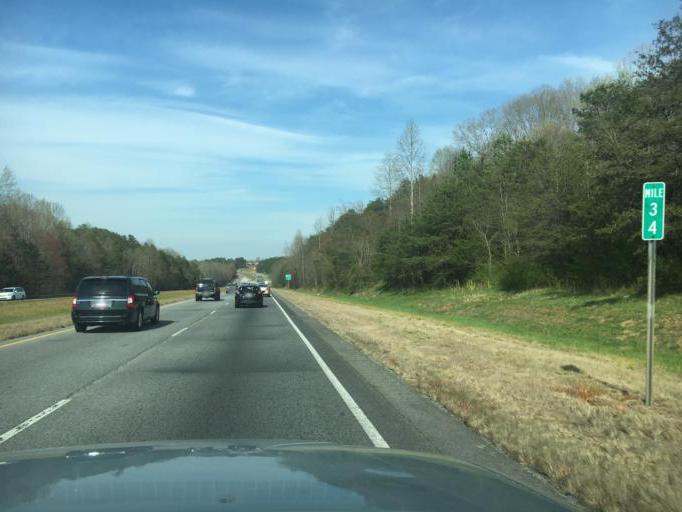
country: US
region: Georgia
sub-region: Hall County
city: Lula
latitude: 34.4106
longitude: -83.6656
